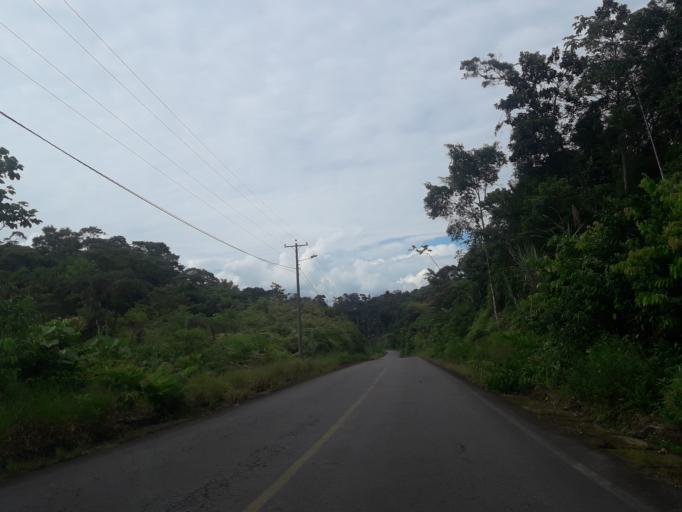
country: EC
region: Napo
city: Tena
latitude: -1.0443
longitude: -77.8983
